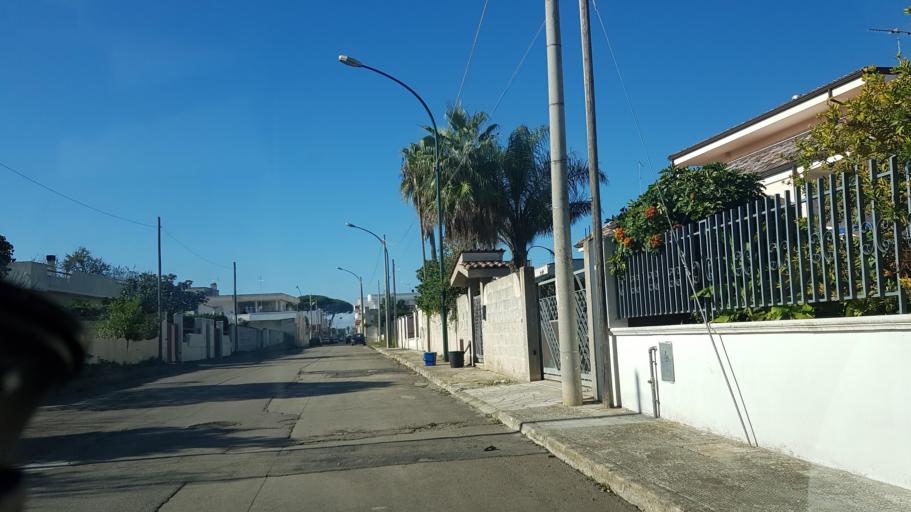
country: IT
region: Apulia
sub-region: Provincia di Lecce
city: Squinzano
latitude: 40.4286
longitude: 18.0471
